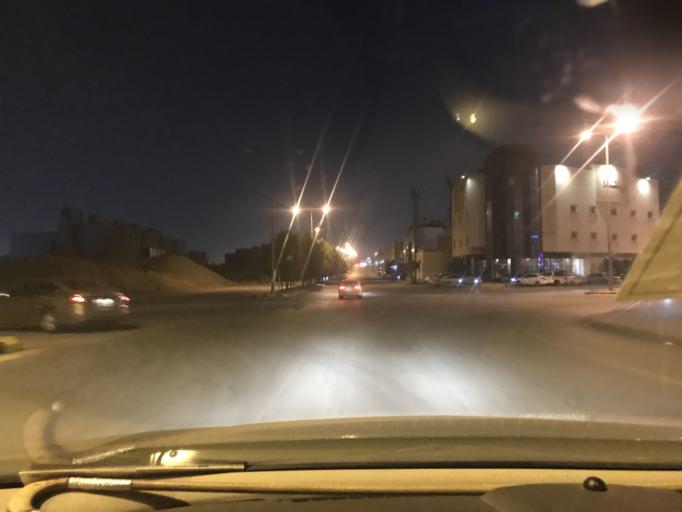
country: SA
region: Ar Riyad
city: Riyadh
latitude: 24.7523
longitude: 46.7544
